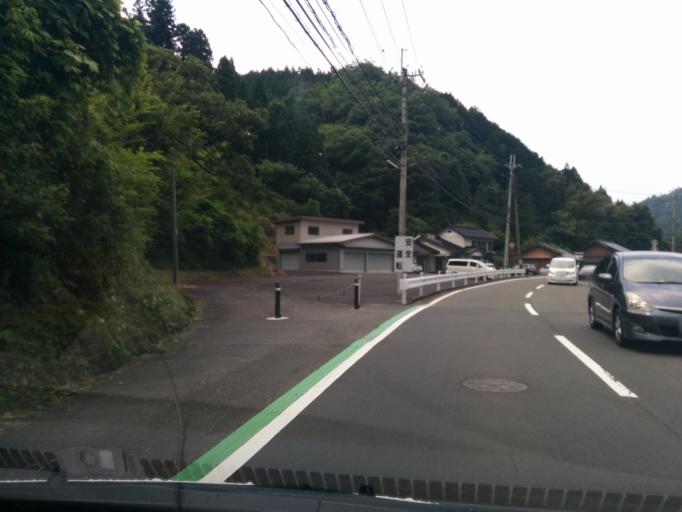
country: JP
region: Kyoto
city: Miyazu
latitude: 35.4179
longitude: 135.1544
